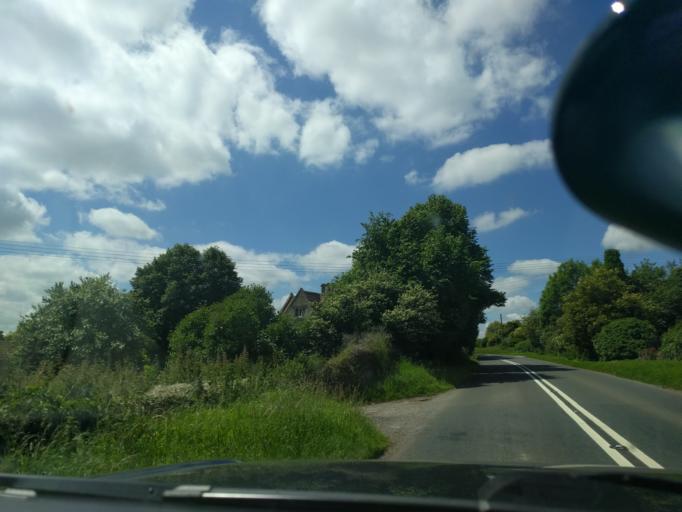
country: GB
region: England
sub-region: Wiltshire
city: Box
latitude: 51.4034
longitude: -2.2244
